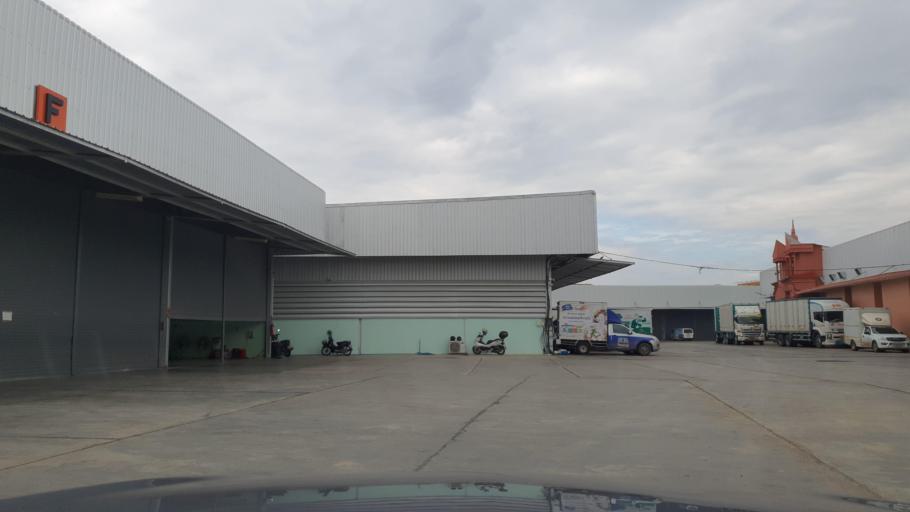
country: TH
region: Chiang Mai
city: Saraphi
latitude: 18.7416
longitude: 99.0077
